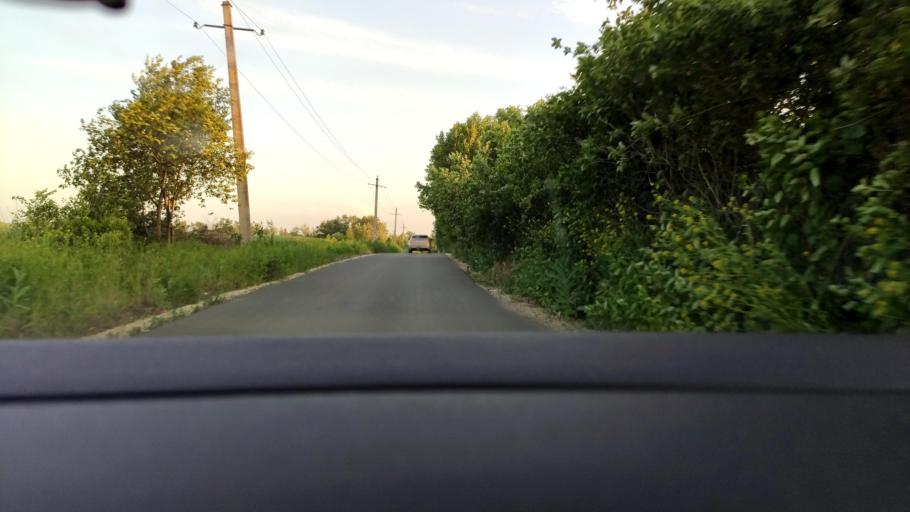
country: RU
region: Voronezj
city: Ramon'
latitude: 51.9055
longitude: 39.1794
